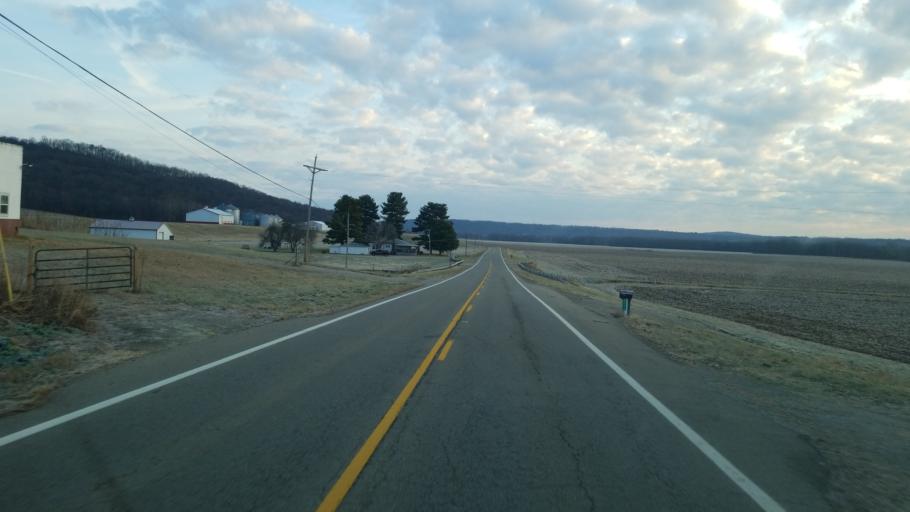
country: US
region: Ohio
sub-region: Ross County
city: Frankfort
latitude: 39.2537
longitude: -83.1955
